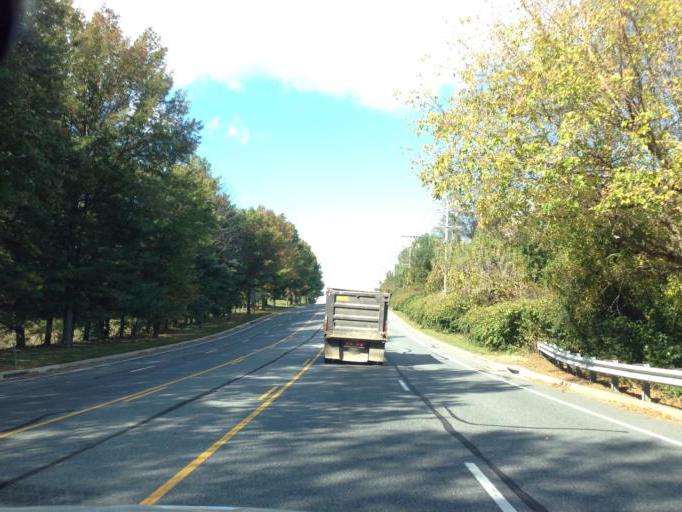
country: US
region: Maryland
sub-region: Baltimore County
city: Hunt Valley
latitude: 39.5167
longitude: -76.6425
